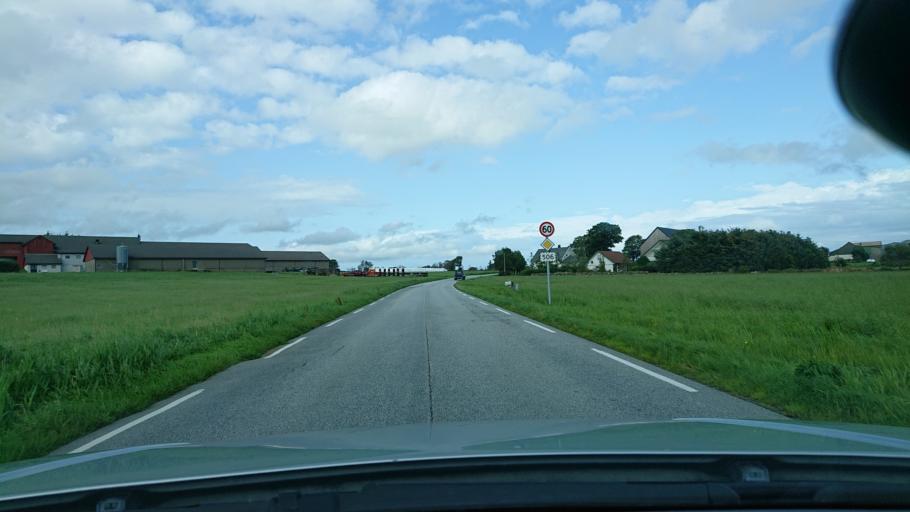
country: NO
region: Rogaland
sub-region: Gjesdal
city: Algard
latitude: 58.6902
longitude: 5.7694
